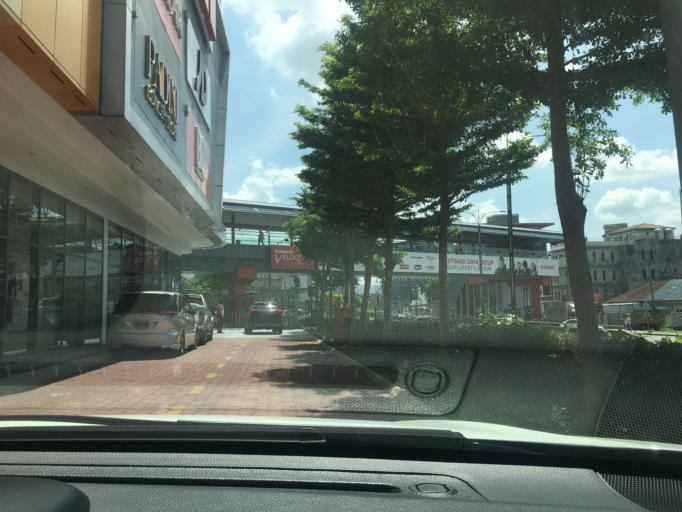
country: MY
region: Kuala Lumpur
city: Kuala Lumpur
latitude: 3.1267
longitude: 101.7246
